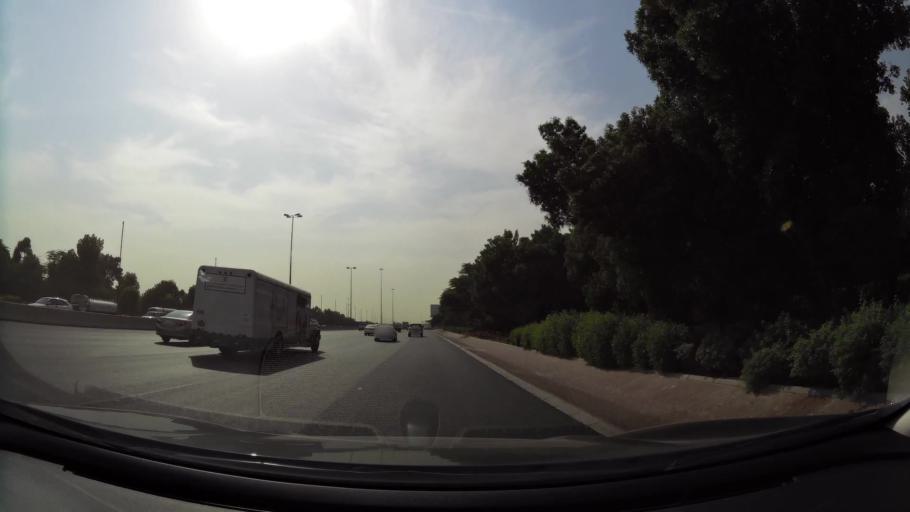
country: KW
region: Al Farwaniyah
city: Janub as Surrah
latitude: 29.2742
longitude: 47.9864
